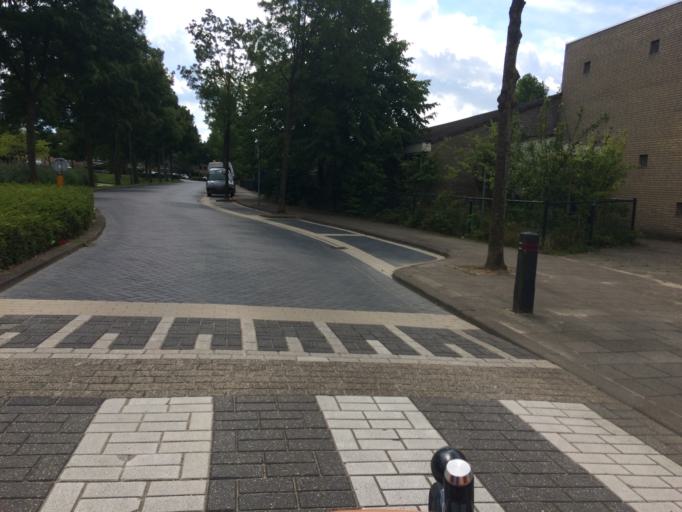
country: NL
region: Gelderland
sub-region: Gemeente Maasdriel
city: Hedel
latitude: 51.7302
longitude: 5.2874
